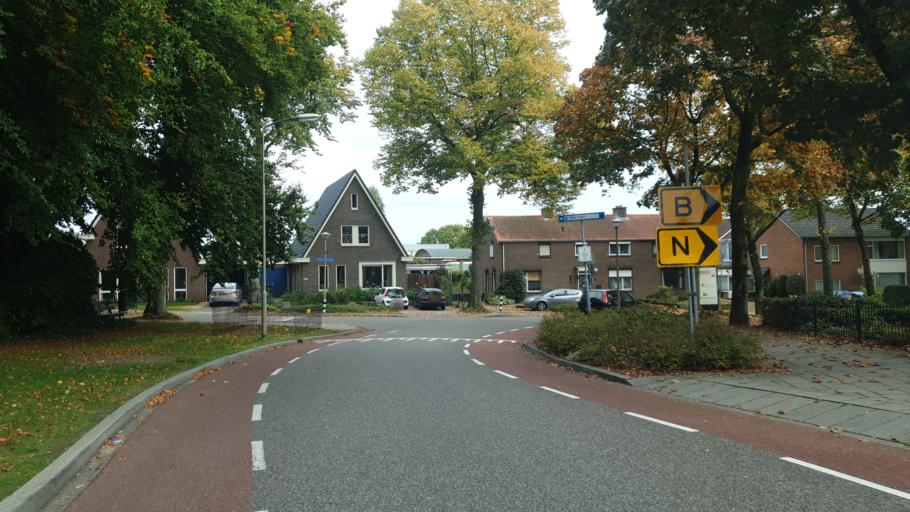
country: NL
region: Gelderland
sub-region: Gemeente Groesbeek
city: Groesbeek
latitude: 51.7751
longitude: 5.9405
